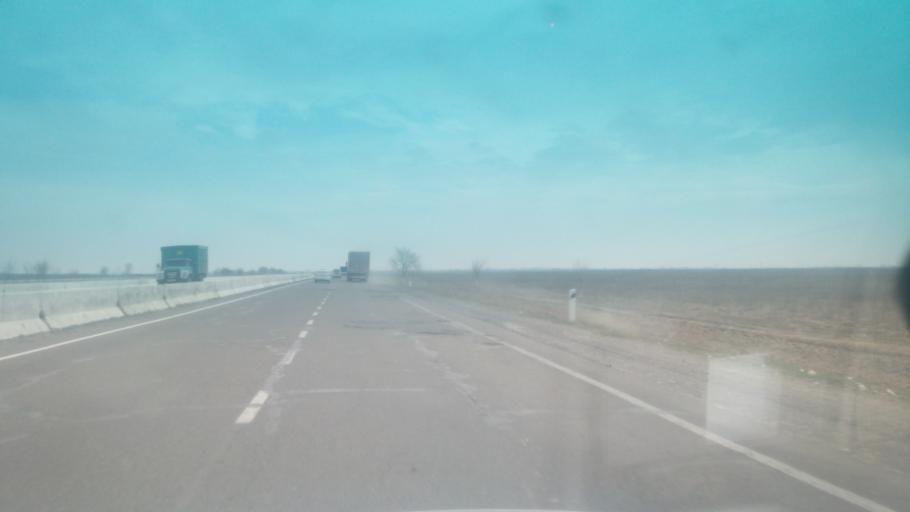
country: KZ
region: Ongtustik Qazaqstan
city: Myrzakent
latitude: 40.5165
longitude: 68.4787
